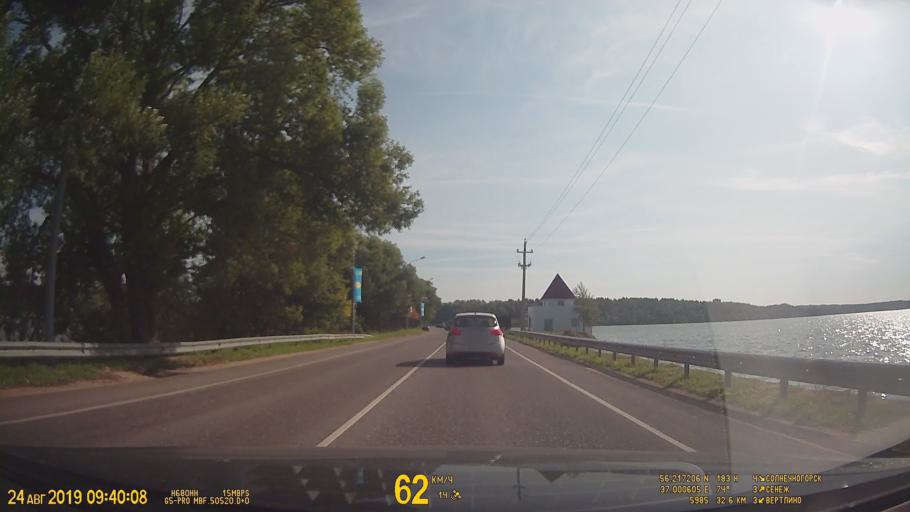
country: RU
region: Moskovskaya
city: Solnechnogorsk
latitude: 56.2173
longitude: 37.0010
